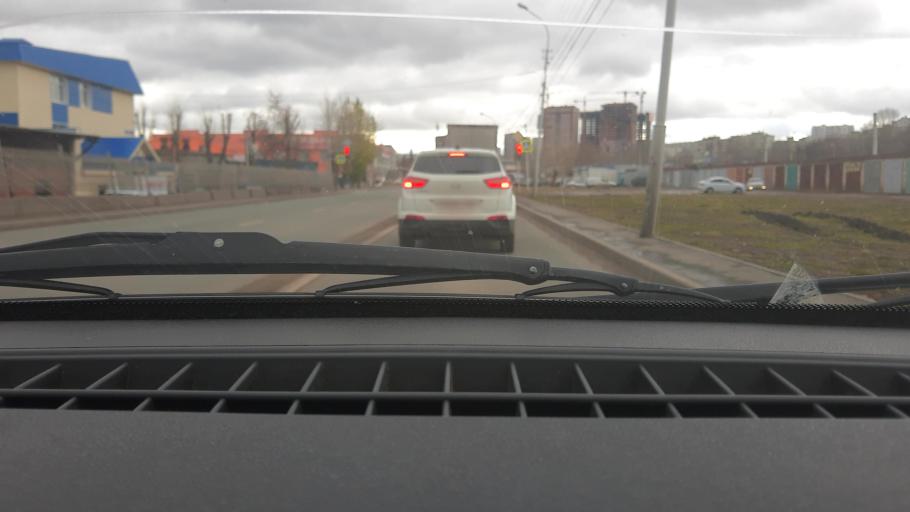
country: RU
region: Bashkortostan
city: Ufa
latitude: 54.7910
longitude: 56.0591
